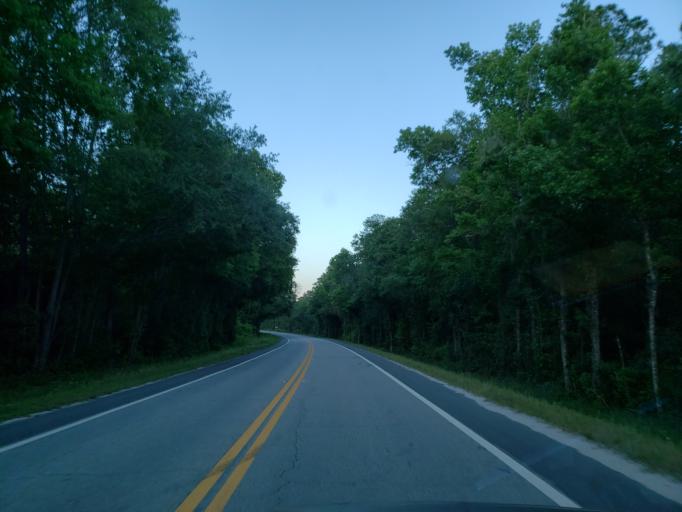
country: US
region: Florida
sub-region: Hamilton County
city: Jasper
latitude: 30.5541
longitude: -83.1062
